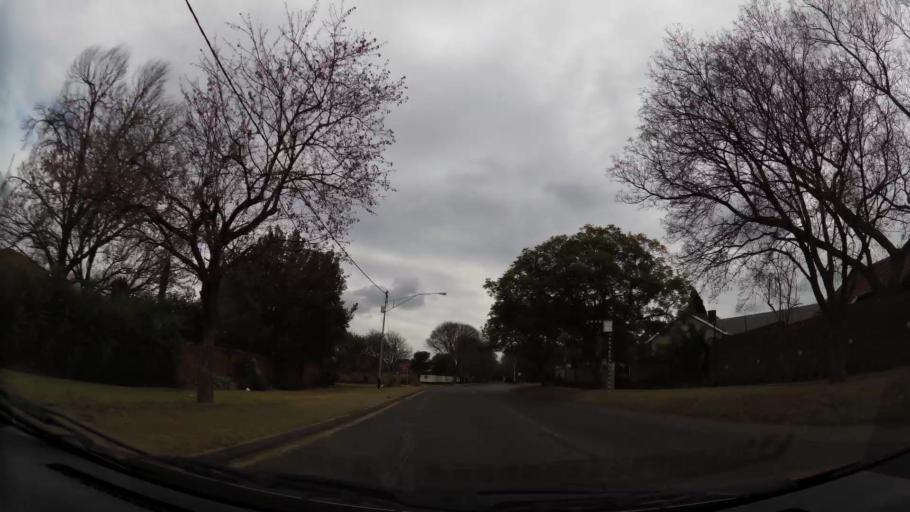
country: ZA
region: Gauteng
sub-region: City of Johannesburg Metropolitan Municipality
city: Johannesburg
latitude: -26.1476
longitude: 27.9932
